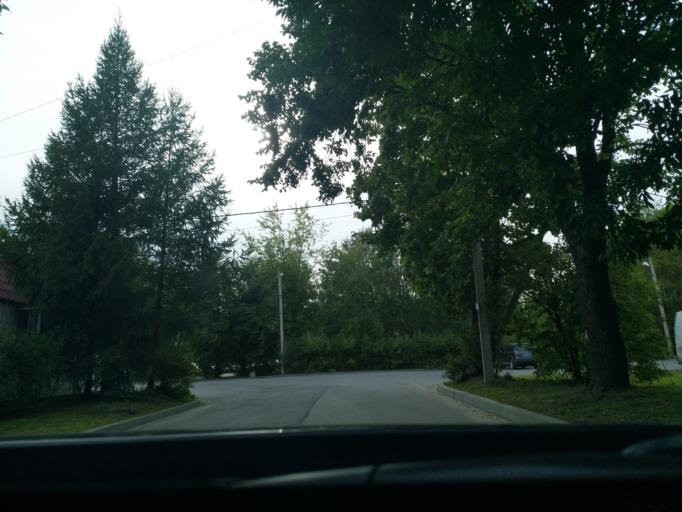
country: RU
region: Leningrad
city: Nikol'skoye
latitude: 59.7030
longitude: 30.7891
